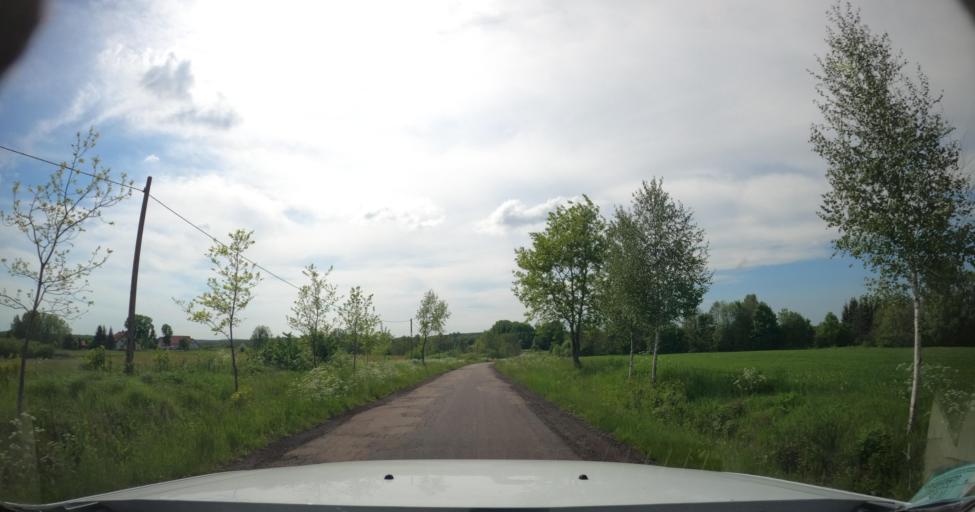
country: PL
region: Warmian-Masurian Voivodeship
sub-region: Powiat lidzbarski
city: Lidzbark Warminski
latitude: 54.1126
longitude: 20.4883
